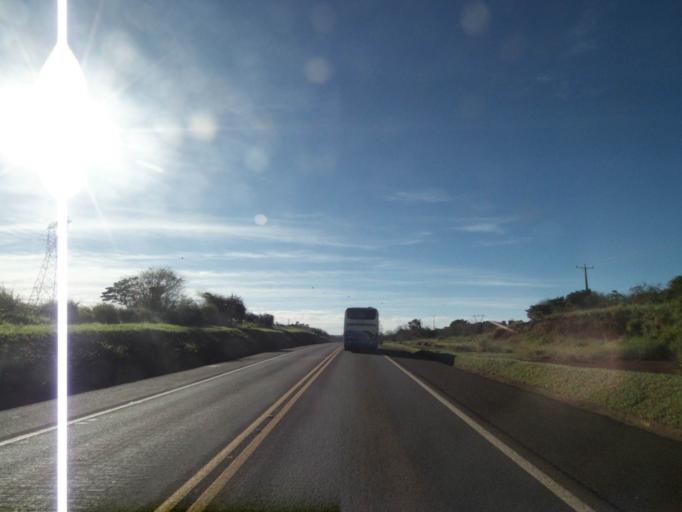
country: BR
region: Parana
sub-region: Cascavel
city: Cascavel
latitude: -25.0292
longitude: -53.5718
